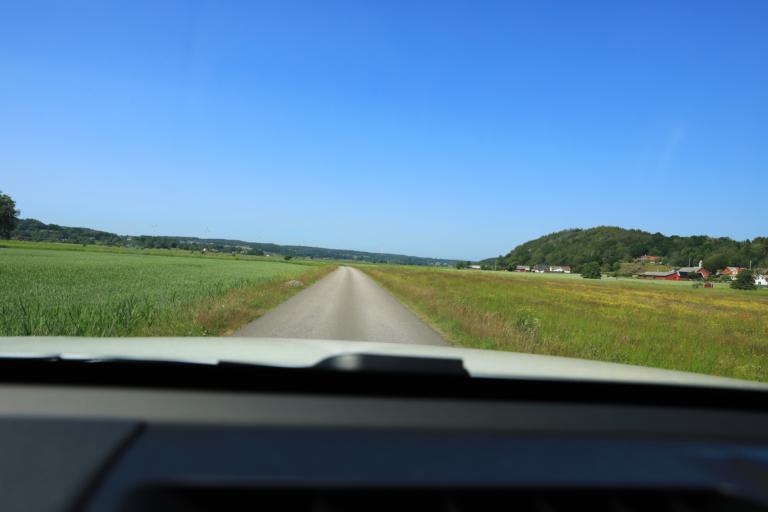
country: SE
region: Halland
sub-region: Varbergs Kommun
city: Varberg
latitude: 57.1680
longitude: 12.3188
